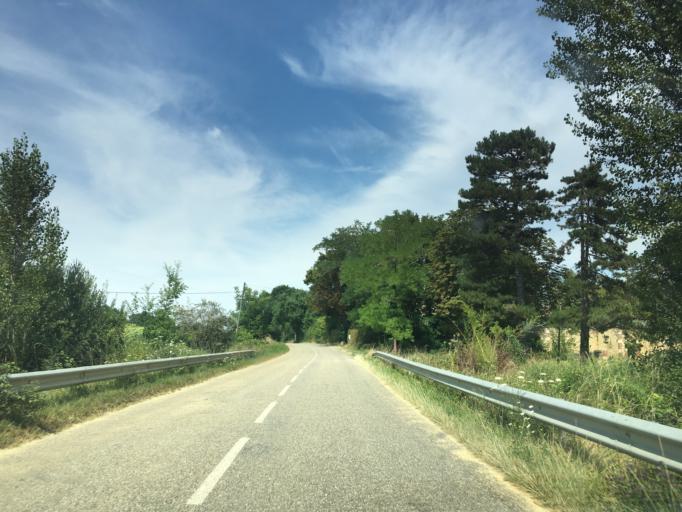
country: FR
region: Midi-Pyrenees
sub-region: Departement du Gers
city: Fleurance
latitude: 43.8998
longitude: 0.7723
